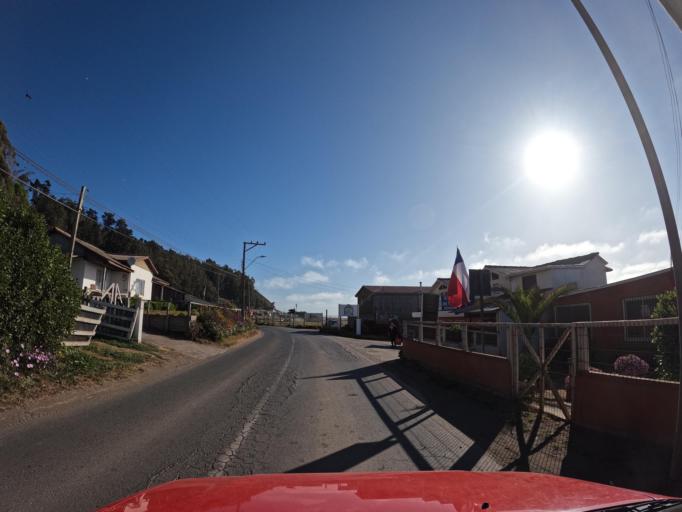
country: CL
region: Maule
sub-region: Provincia de Talca
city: Constitucion
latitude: -34.8877
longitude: -72.1711
